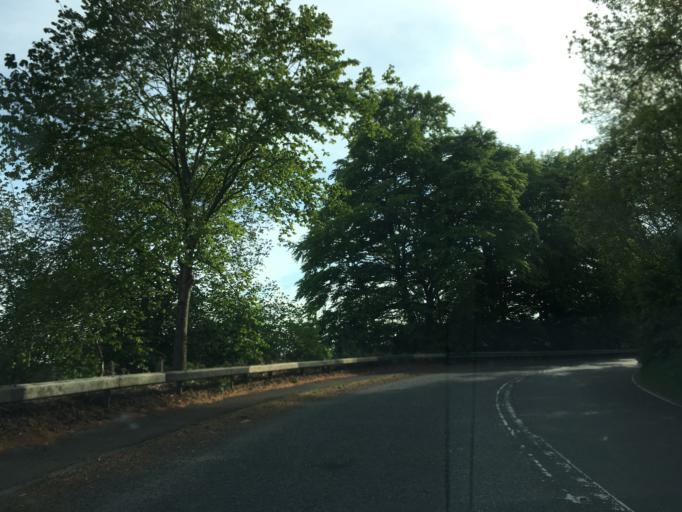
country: GB
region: Scotland
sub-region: Midlothian
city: Penicuik
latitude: 55.8186
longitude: -3.2208
